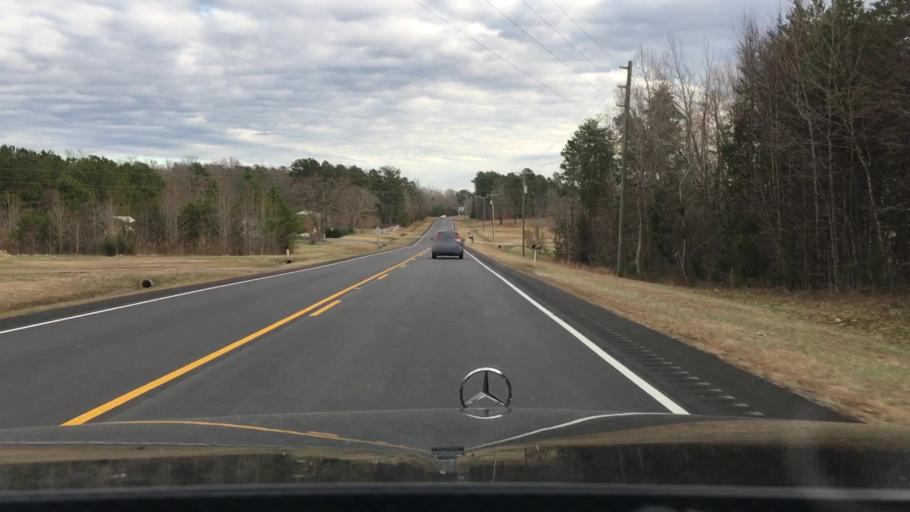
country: US
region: North Carolina
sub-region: Caswell County
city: Yanceyville
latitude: 36.2743
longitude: -79.2048
